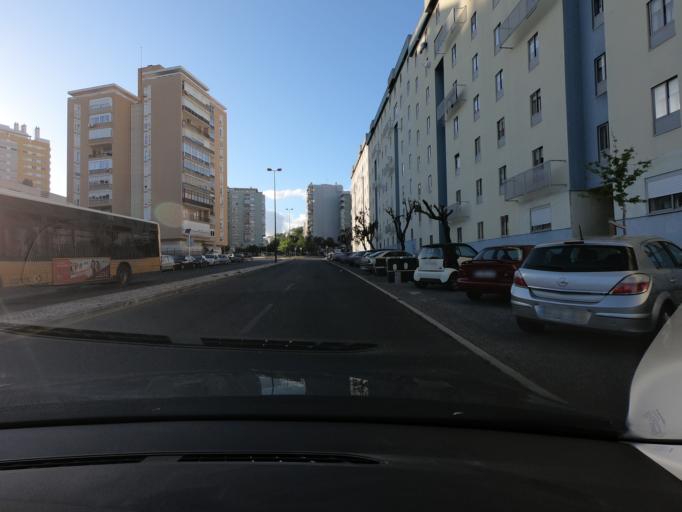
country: PT
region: Lisbon
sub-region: Lisbon
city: Lisbon
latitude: 38.7270
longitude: -9.1232
